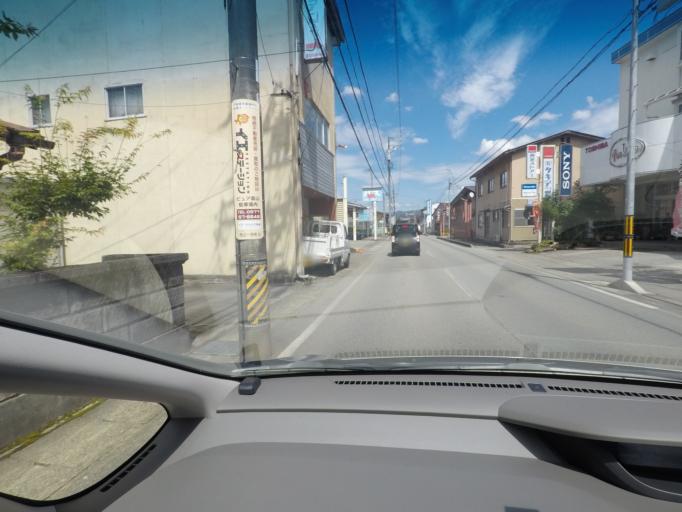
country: JP
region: Gifu
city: Takayama
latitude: 36.1370
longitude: 137.2499
